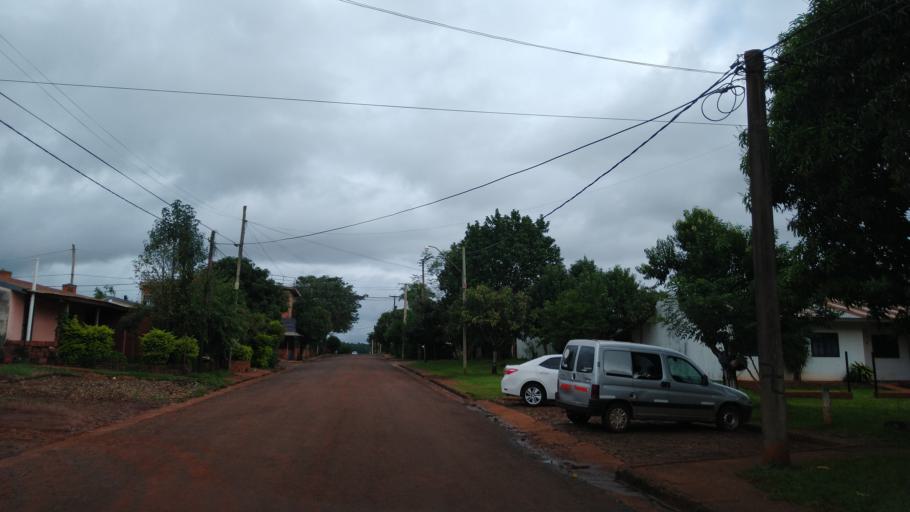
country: AR
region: Misiones
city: Capiovi
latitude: -26.9325
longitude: -55.0554
